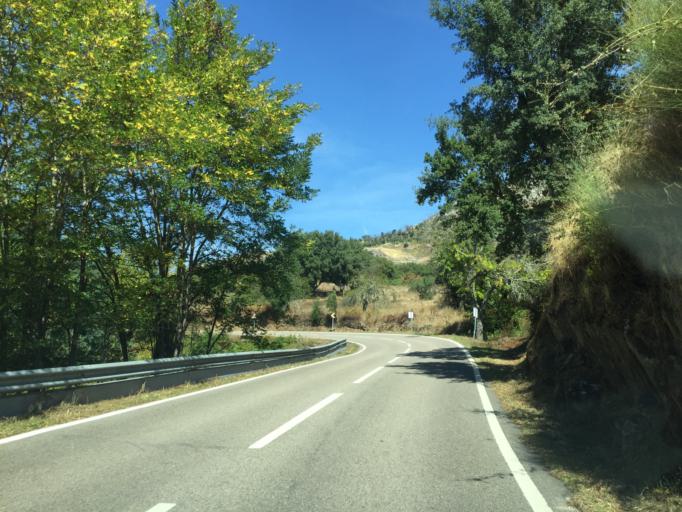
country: PT
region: Portalegre
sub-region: Marvao
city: Marvao
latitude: 39.3865
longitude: -7.3851
